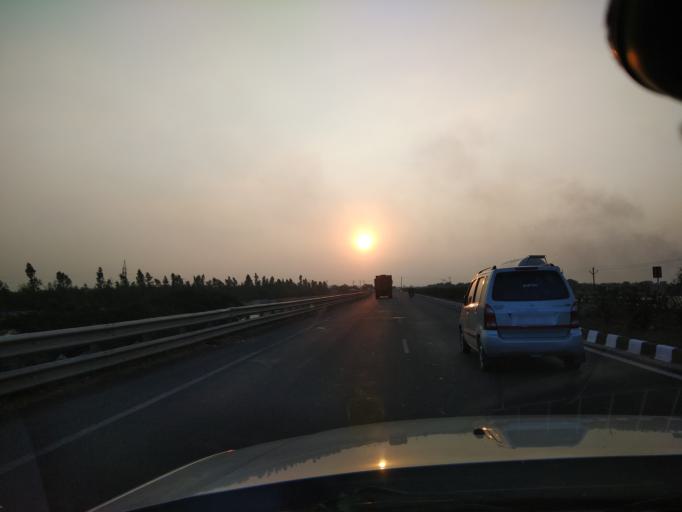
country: IN
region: Gujarat
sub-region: Jamnagar
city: Bedi
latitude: 22.4453
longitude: 70.0027
